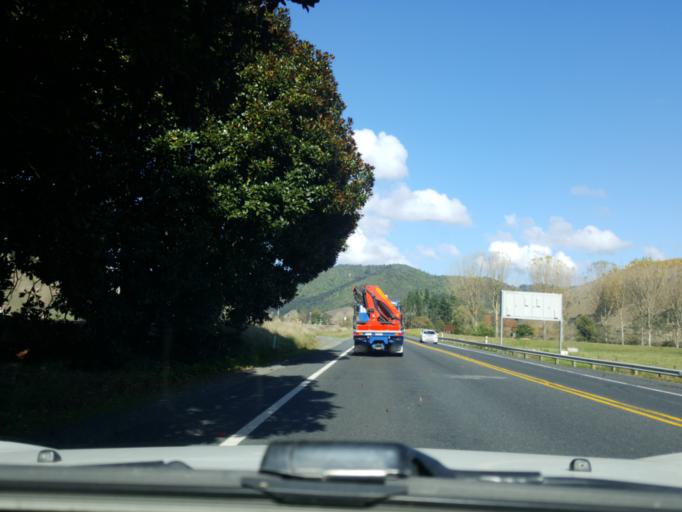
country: NZ
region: Waikato
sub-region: Waikato District
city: Ngaruawahia
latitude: -37.5860
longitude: 175.1596
